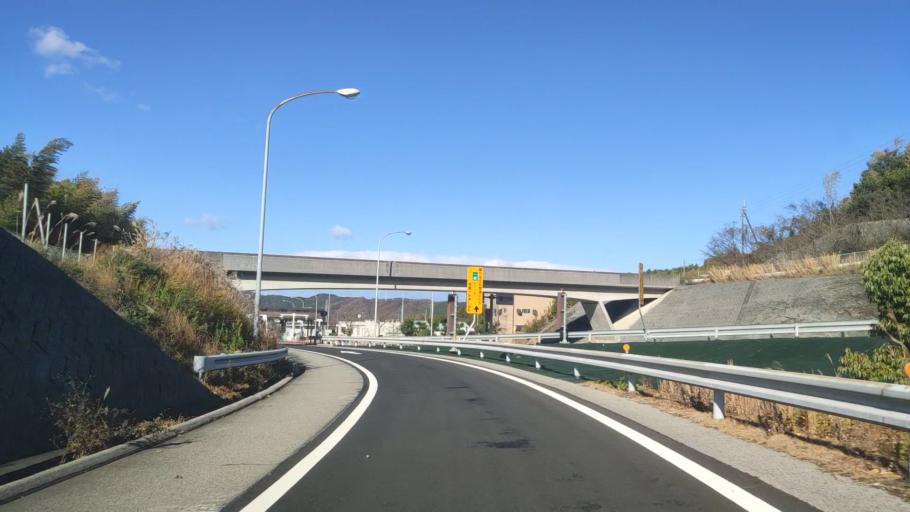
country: JP
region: Ehime
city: Saijo
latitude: 33.9129
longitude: 133.2371
